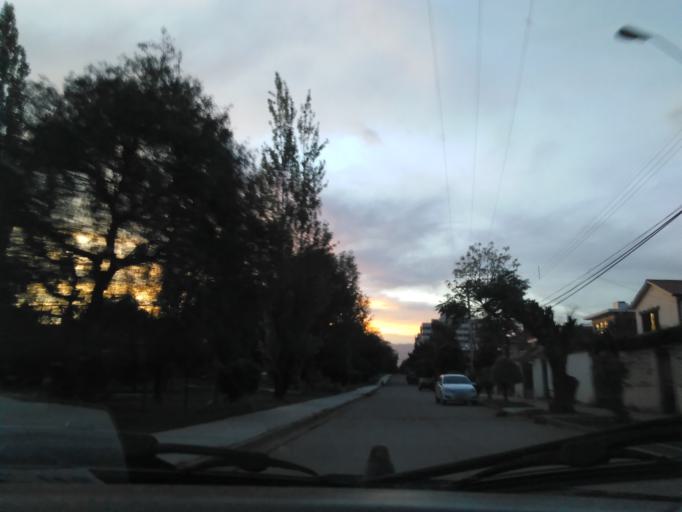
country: BO
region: Cochabamba
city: Cochabamba
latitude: -17.3700
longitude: -66.1660
